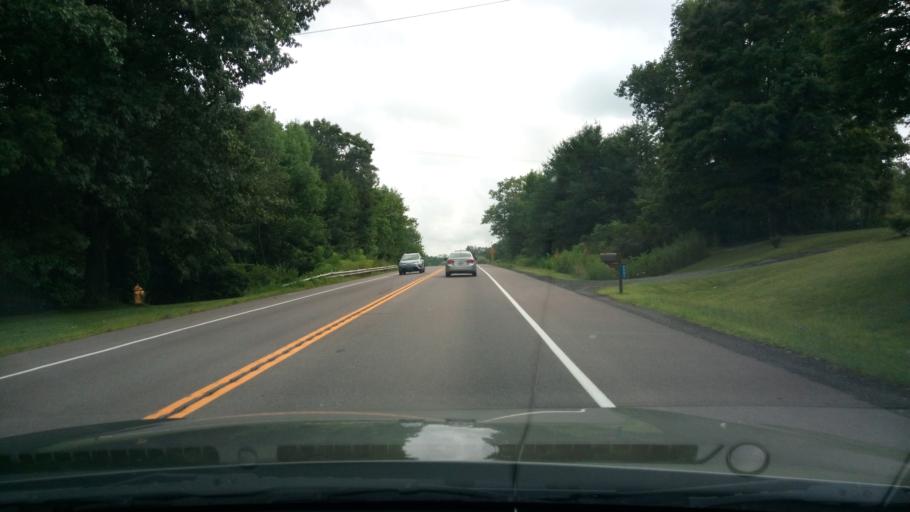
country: US
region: New York
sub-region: Tompkins County
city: Northwest Ithaca
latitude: 42.3515
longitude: -76.6112
